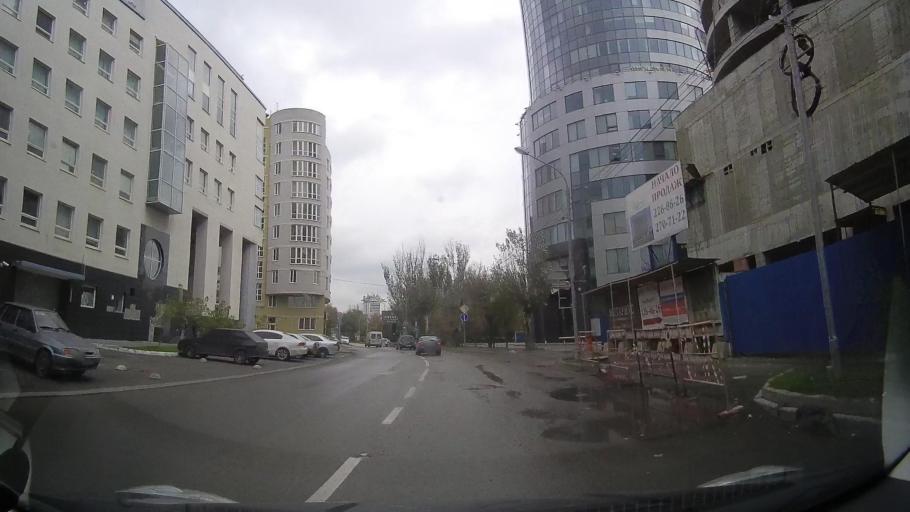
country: RU
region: Rostov
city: Rostov-na-Donu
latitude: 47.2128
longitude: 39.7048
